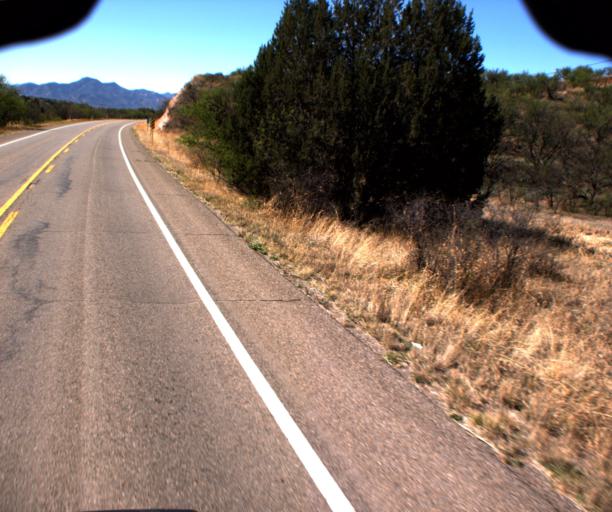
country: US
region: Arizona
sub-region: Santa Cruz County
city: Rio Rico
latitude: 31.6345
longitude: -110.7134
